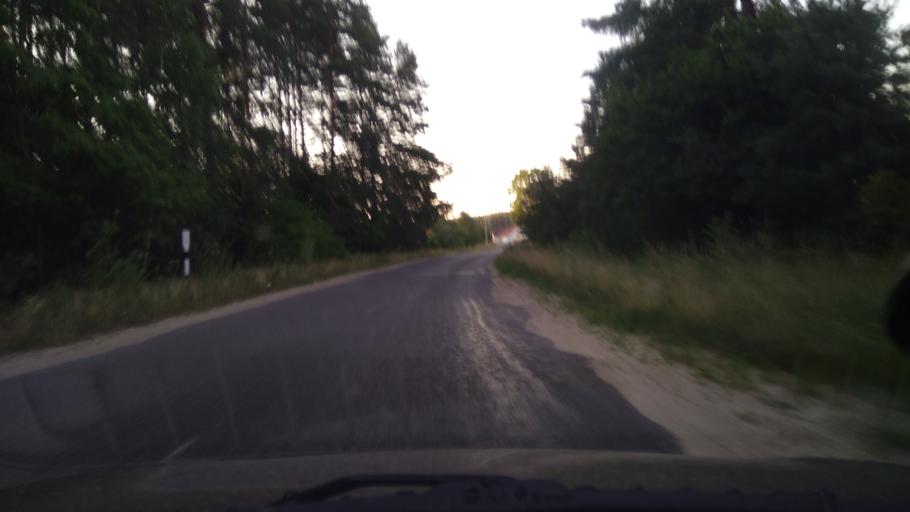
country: BY
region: Brest
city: Nyakhachava
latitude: 52.6062
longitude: 25.0856
